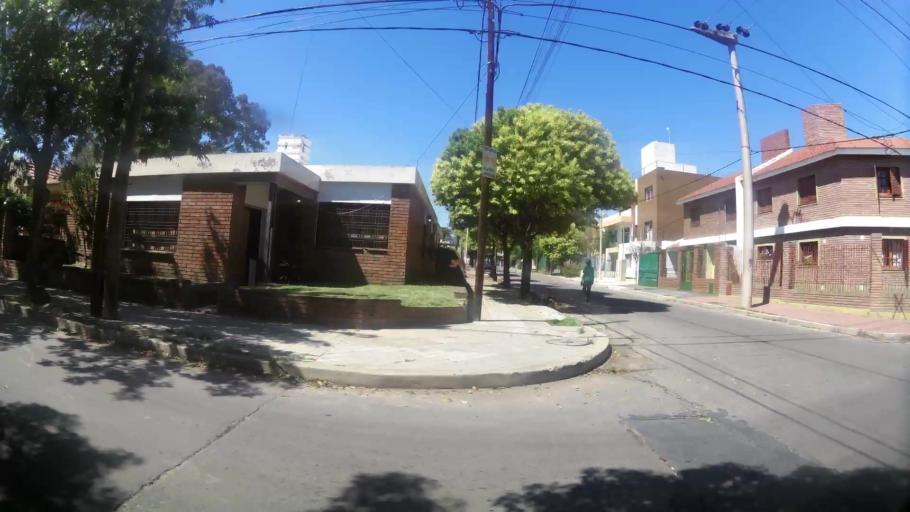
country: AR
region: Cordoba
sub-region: Departamento de Capital
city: Cordoba
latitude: -31.4192
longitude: -64.2145
